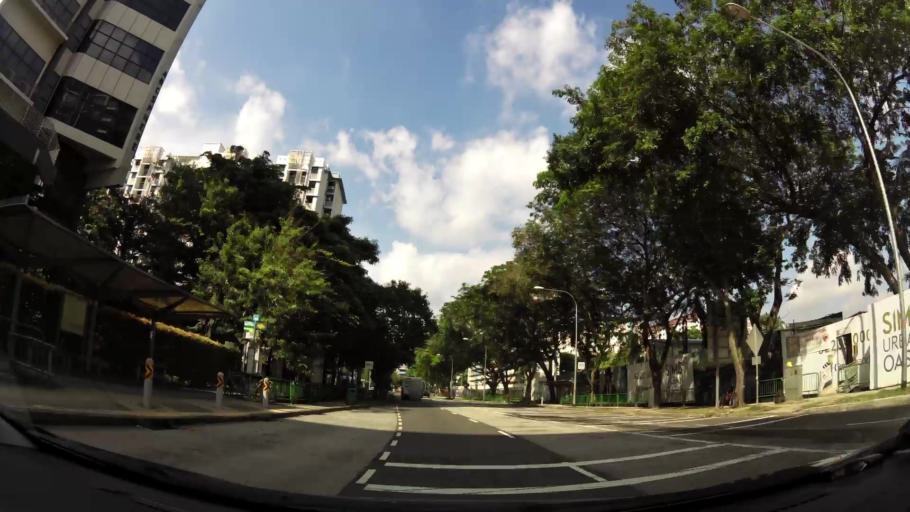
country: SG
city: Singapore
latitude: 1.3185
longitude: 103.8803
